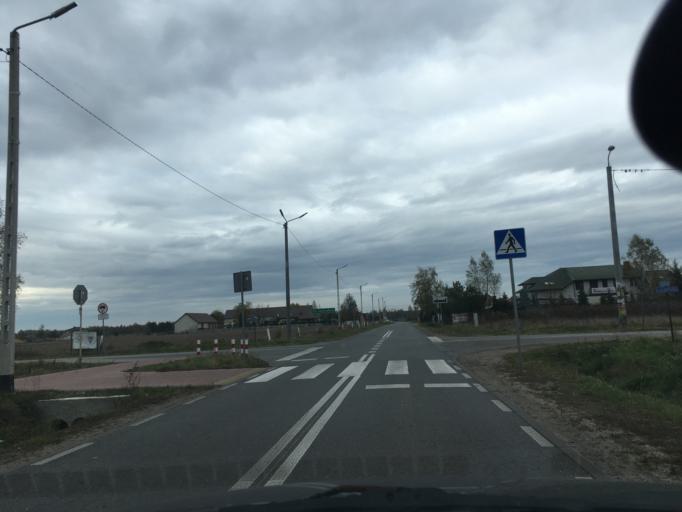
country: PL
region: Lodz Voivodeship
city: Zabia Wola
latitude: 52.0199
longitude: 20.7306
